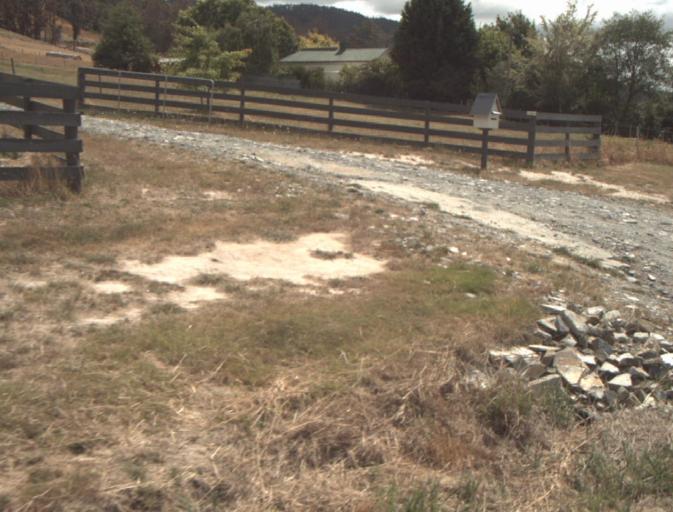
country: AU
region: Tasmania
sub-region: Launceston
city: Mayfield
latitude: -41.2390
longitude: 147.1353
